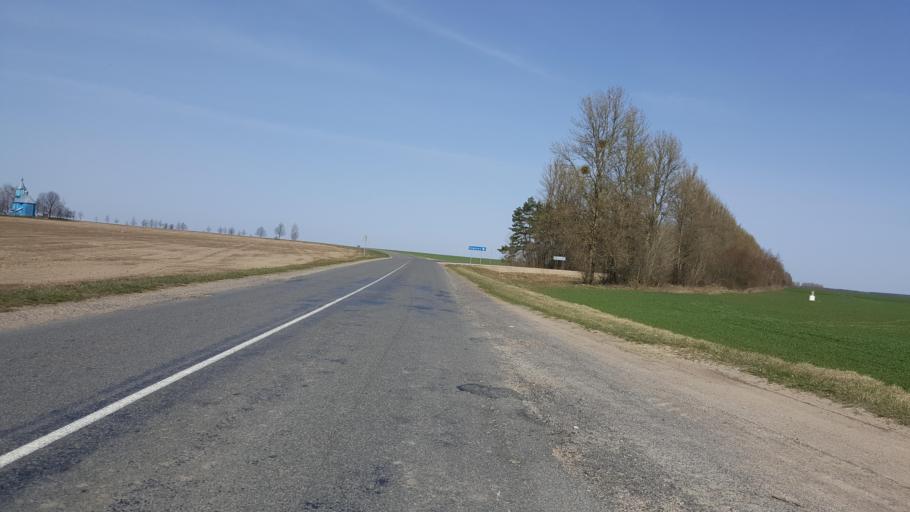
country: BY
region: Brest
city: Kamyanyets
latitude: 52.4439
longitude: 23.7394
